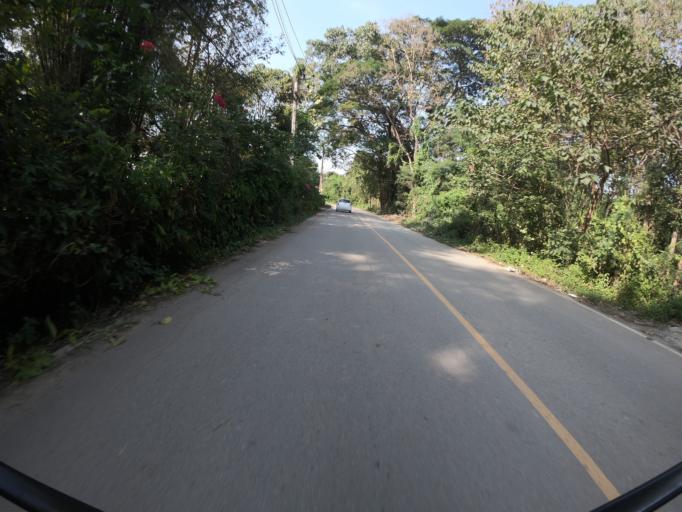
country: TH
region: Chiang Mai
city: San Sai
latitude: 18.8428
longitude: 99.0055
